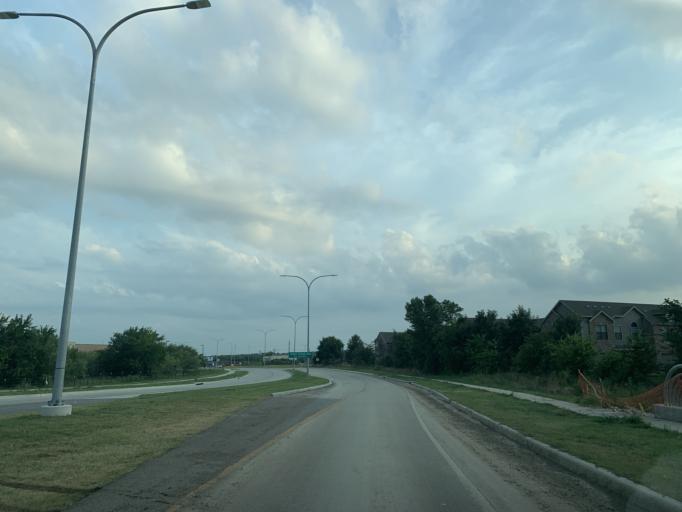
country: US
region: Texas
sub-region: Tarrant County
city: Keller
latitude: 32.9344
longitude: -97.2719
